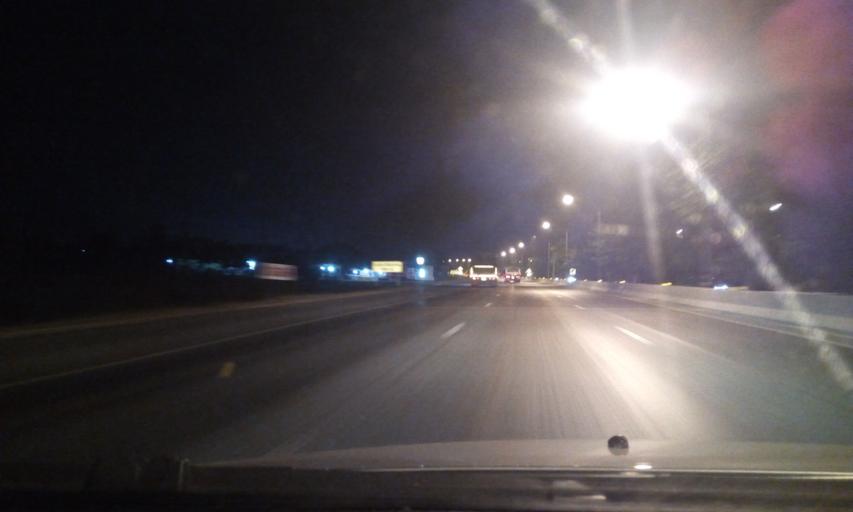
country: TH
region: Sing Buri
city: Phrom Buri
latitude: 14.7762
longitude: 100.4522
